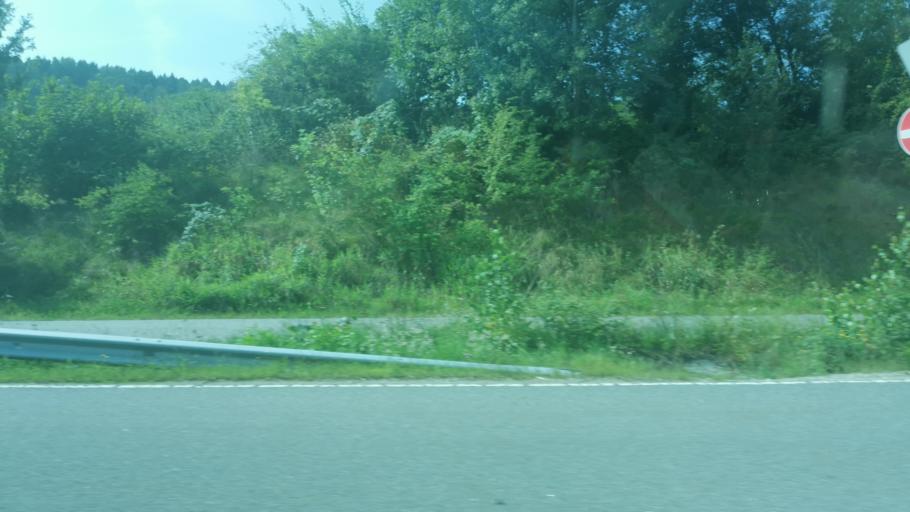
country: DE
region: Bavaria
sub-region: Upper Palatinate
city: Chamerau
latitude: 49.2080
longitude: 12.7267
